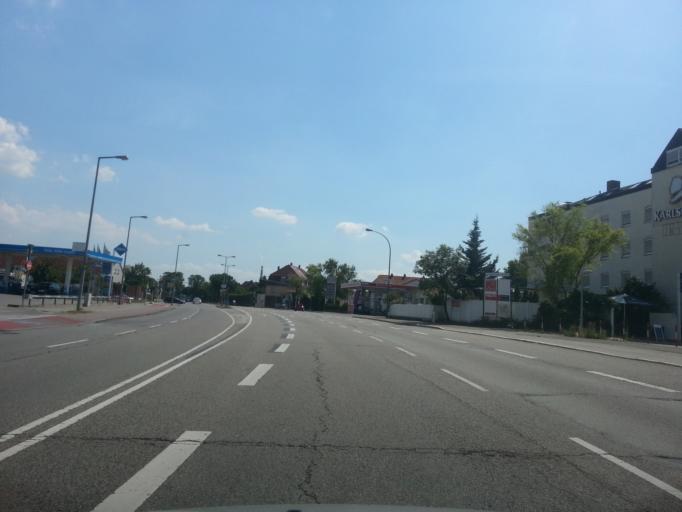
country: DE
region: Hesse
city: Lampertheim
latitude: 49.5506
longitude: 8.4486
